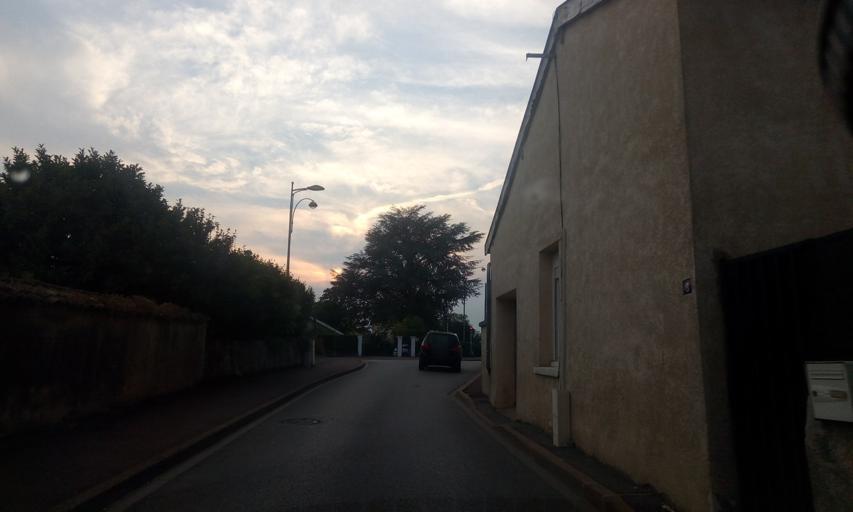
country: FR
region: Rhone-Alpes
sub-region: Departement du Rhone
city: Genas
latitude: 45.7248
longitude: 5.0024
